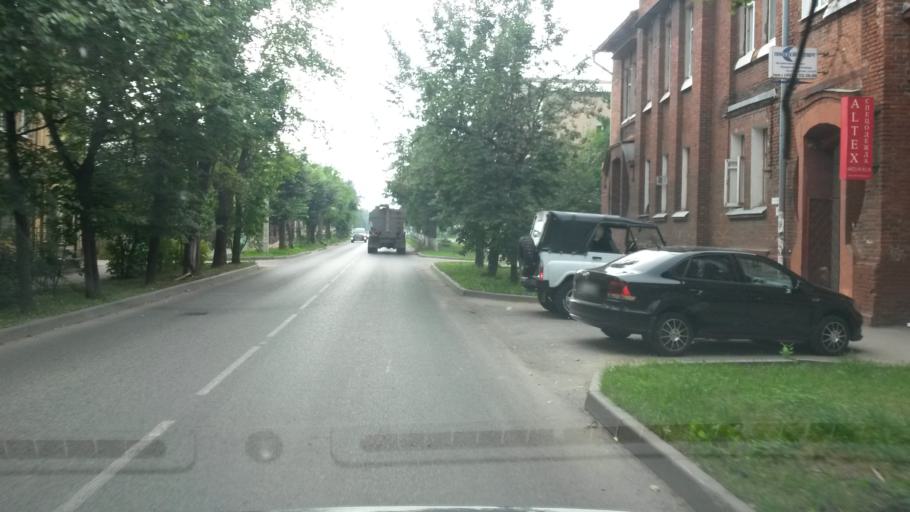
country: RU
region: Ivanovo
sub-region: Gorod Ivanovo
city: Ivanovo
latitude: 56.9951
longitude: 40.9728
